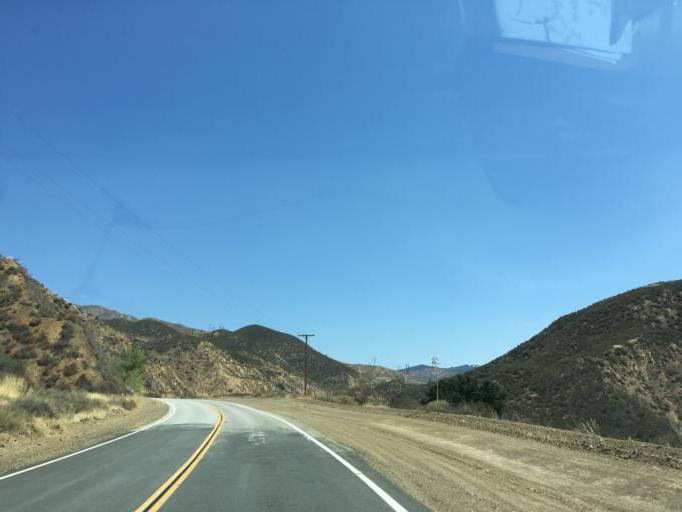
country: US
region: California
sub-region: Los Angeles County
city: Green Valley
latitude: 34.5767
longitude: -118.4598
